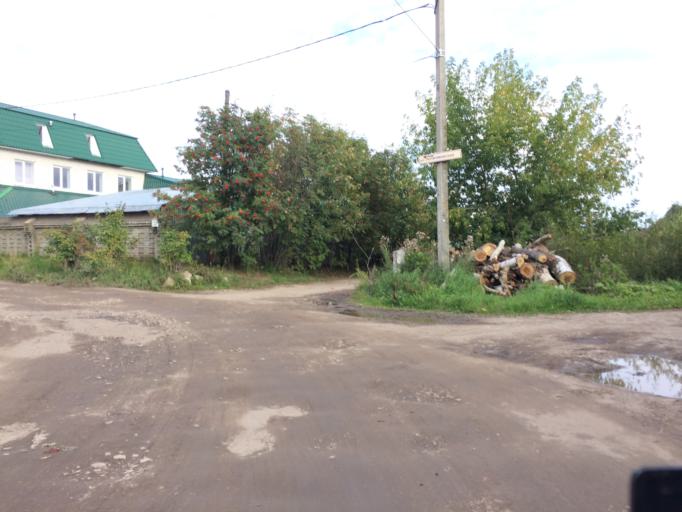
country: RU
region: Mariy-El
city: Yoshkar-Ola
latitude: 56.6541
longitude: 48.0128
